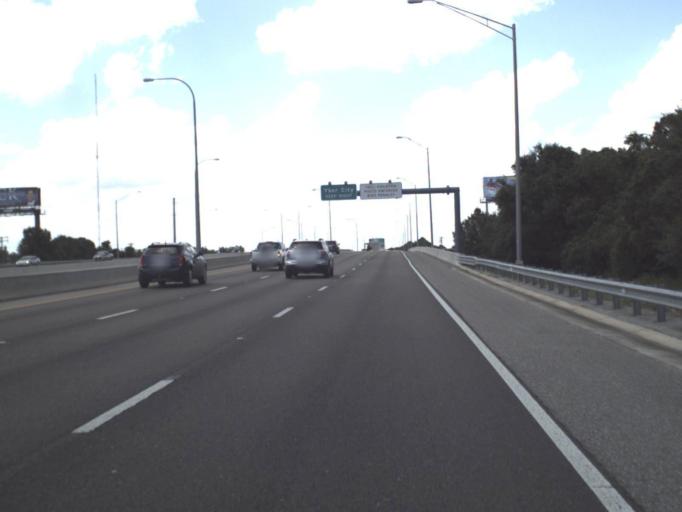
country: US
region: Florida
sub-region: Hillsborough County
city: Palm River-Clair Mel
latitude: 27.9381
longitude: -82.3589
